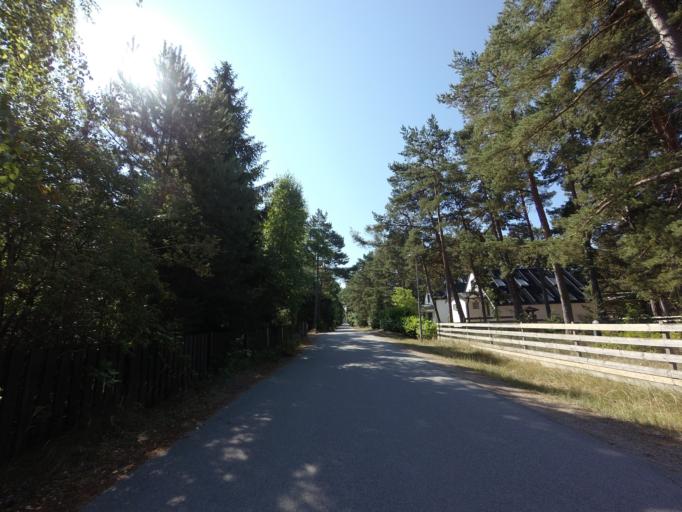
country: SE
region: Skane
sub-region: Vellinge Kommun
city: Ljunghusen
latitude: 55.3987
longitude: 12.9323
